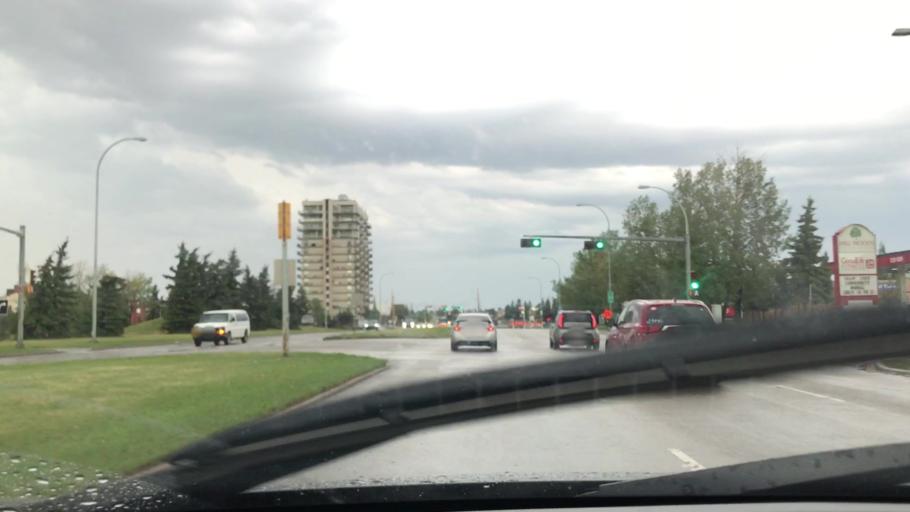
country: CA
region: Alberta
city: Edmonton
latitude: 53.4559
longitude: -113.4344
